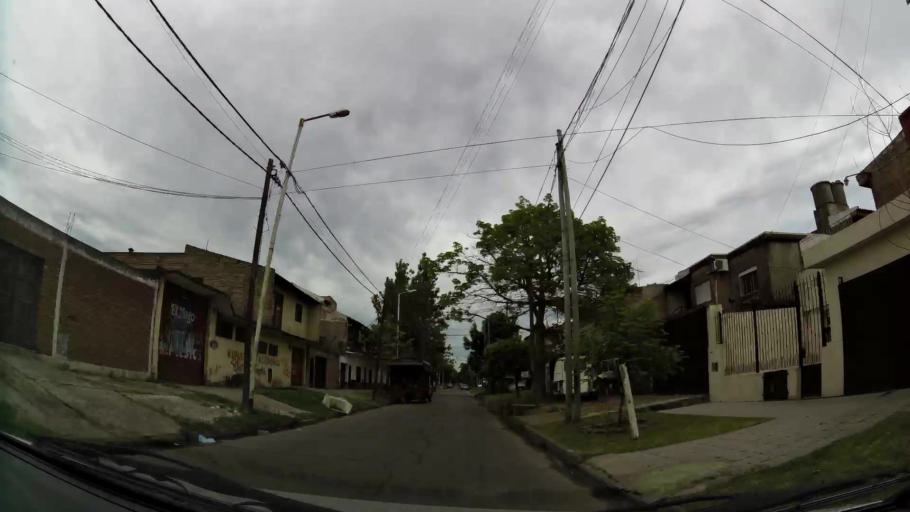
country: AR
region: Buenos Aires
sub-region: Partido de Avellaneda
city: Avellaneda
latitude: -34.6767
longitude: -58.3720
